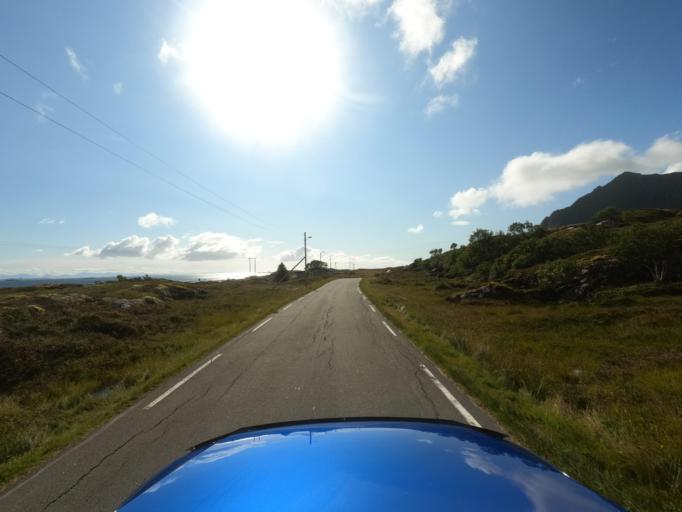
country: NO
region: Nordland
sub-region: Vestvagoy
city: Evjen
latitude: 68.2106
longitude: 14.0546
